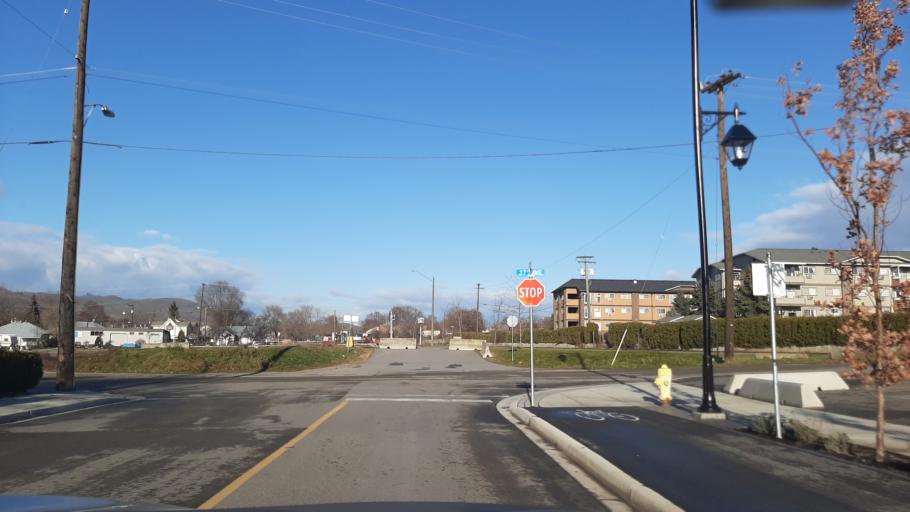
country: CA
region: British Columbia
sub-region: Regional District of North Okanagan
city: Vernon
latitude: 50.2686
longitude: -119.2708
